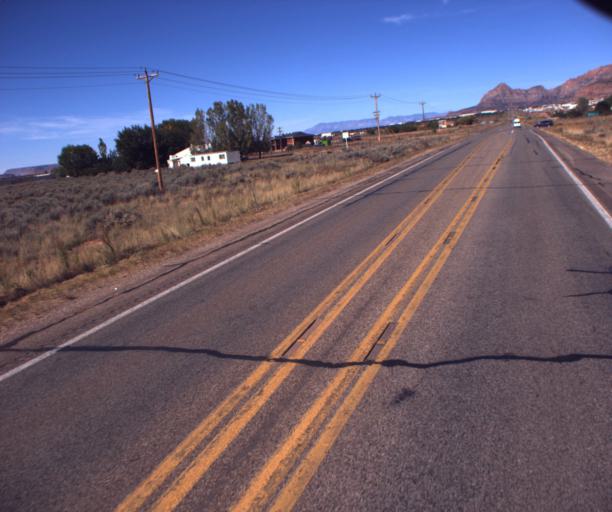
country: US
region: Arizona
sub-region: Mohave County
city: Colorado City
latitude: 36.9821
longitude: -112.9842
